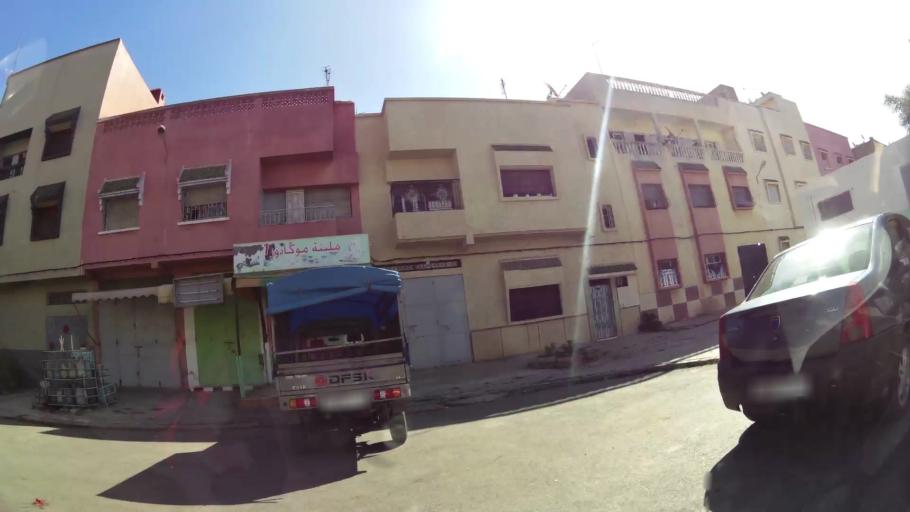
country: MA
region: Rabat-Sale-Zemmour-Zaer
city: Sale
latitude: 34.0671
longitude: -6.7974
